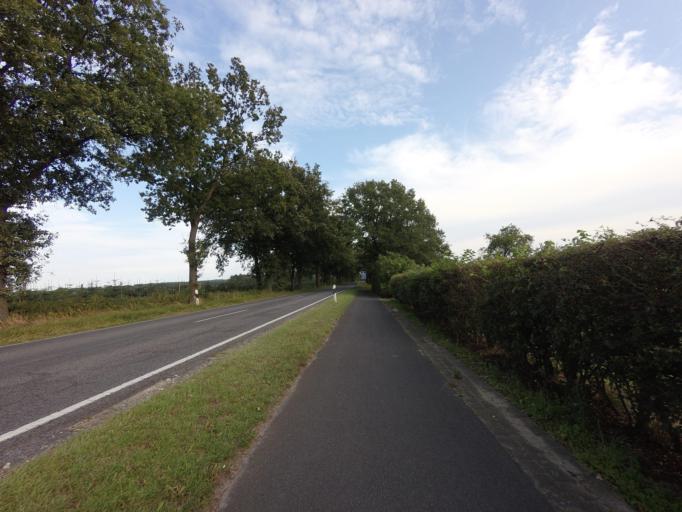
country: DE
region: Lower Saxony
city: Wielen
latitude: 52.5496
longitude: 6.6883
